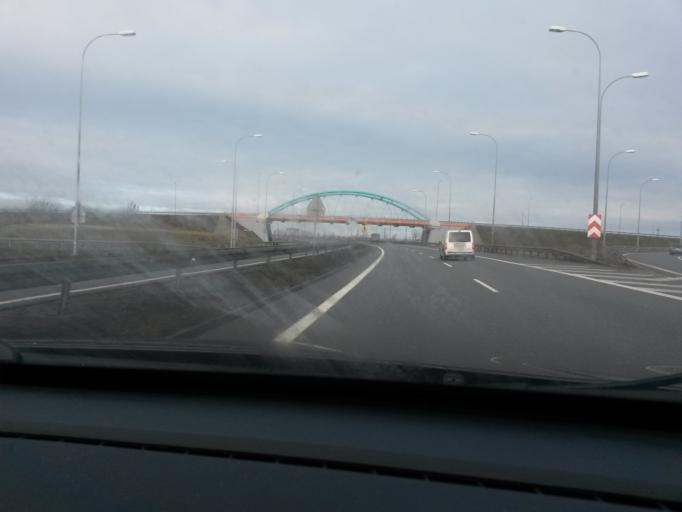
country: PL
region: Pomeranian Voivodeship
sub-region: Powiat nowodworski
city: Nowy Dwor Gdanski
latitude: 54.2115
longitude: 19.1045
